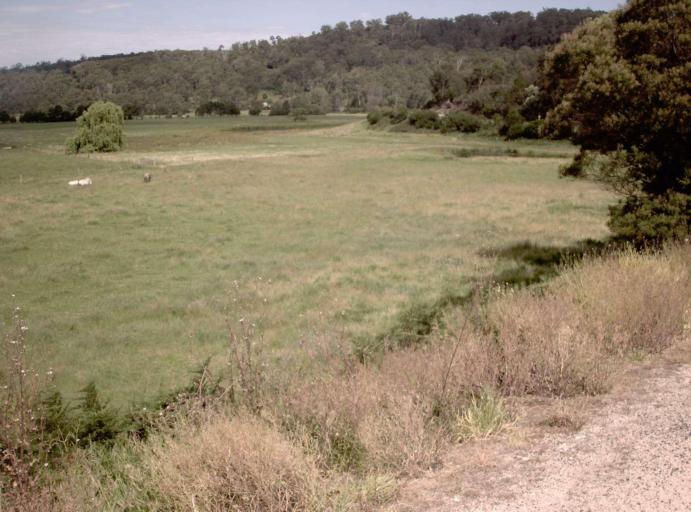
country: AU
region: New South Wales
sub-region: Bega Valley
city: Eden
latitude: -37.4770
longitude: 149.5959
